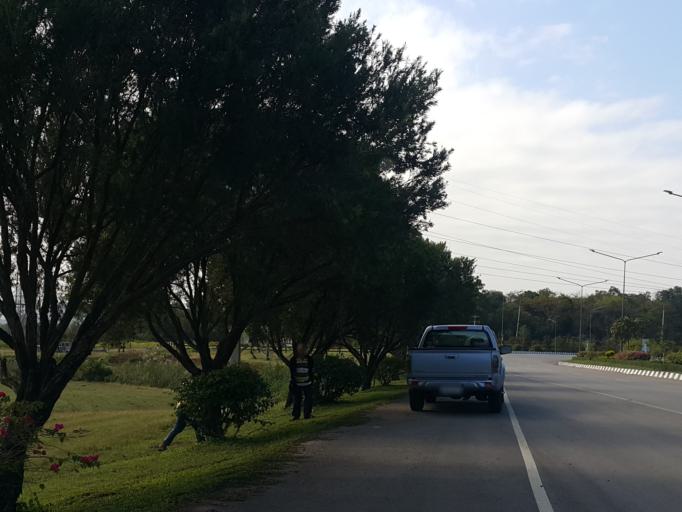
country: TH
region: Lampang
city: Mae Mo
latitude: 18.2978
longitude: 99.7407
